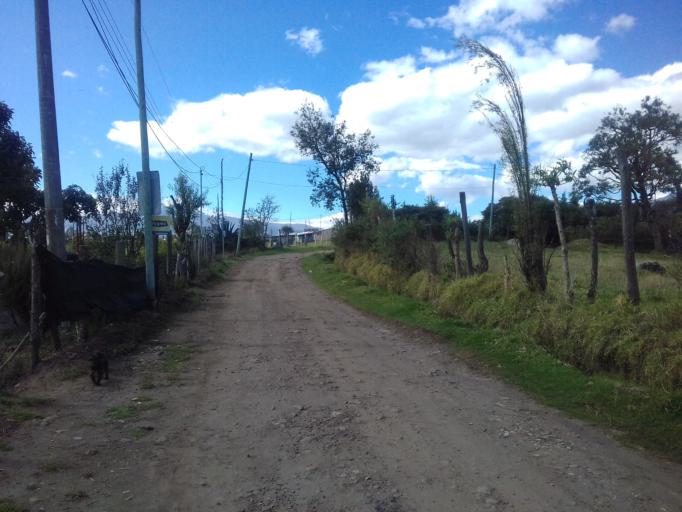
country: EC
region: Pichincha
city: Sangolqui
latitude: -0.3504
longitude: -78.4033
